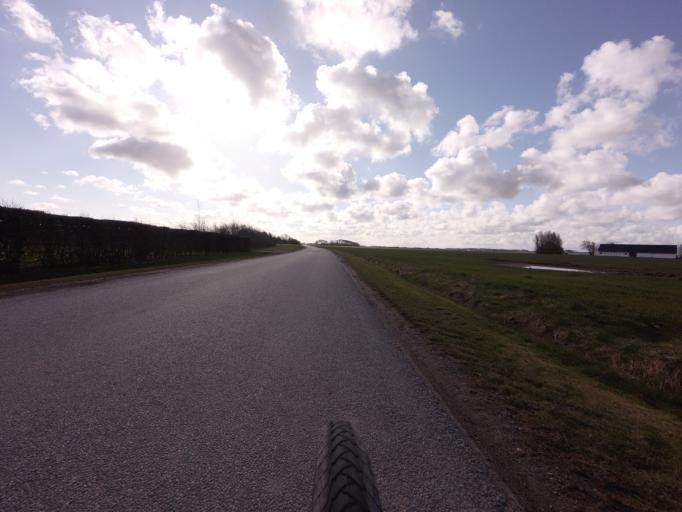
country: DK
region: North Denmark
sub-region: Hjorring Kommune
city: Vra
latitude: 57.3335
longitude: 9.8700
